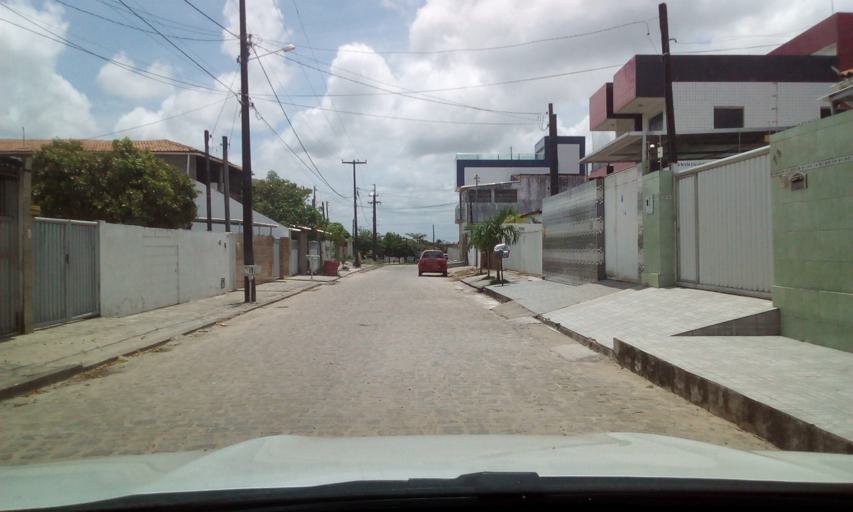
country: BR
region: Paraiba
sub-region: Joao Pessoa
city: Joao Pessoa
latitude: -7.1715
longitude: -34.8844
